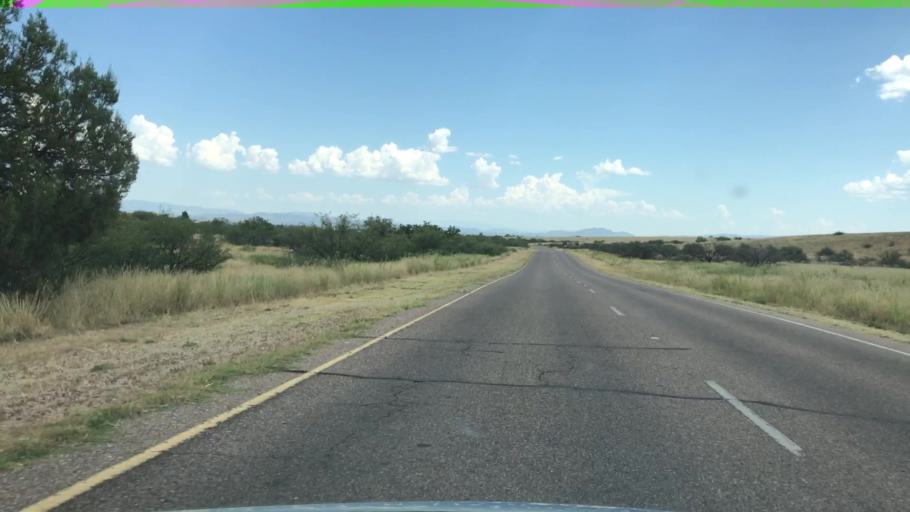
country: US
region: Arizona
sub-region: Cochise County
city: Sierra Vista
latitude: 31.5432
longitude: -110.3329
